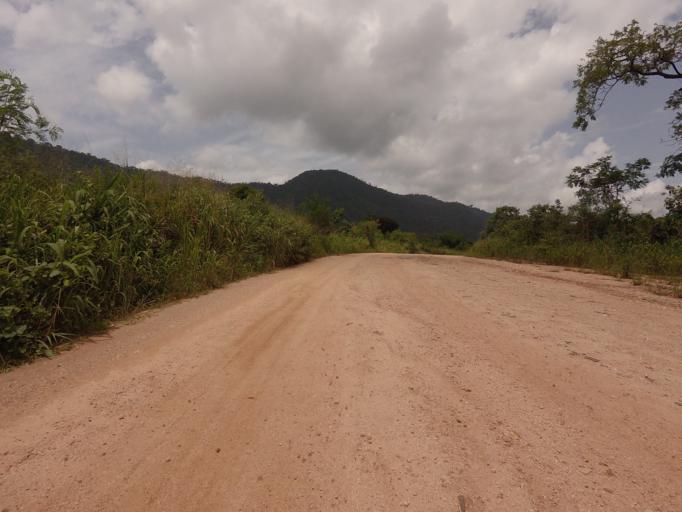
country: GH
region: Volta
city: Ho
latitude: 6.7712
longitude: 0.3644
